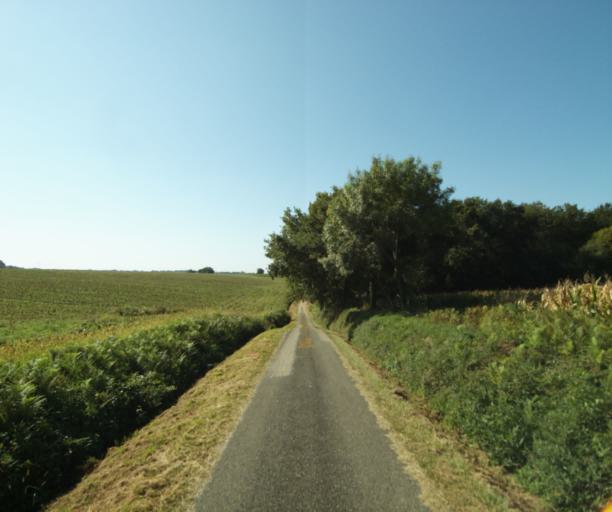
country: FR
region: Aquitaine
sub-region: Departement des Landes
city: Gabarret
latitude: 43.9479
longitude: -0.0006
